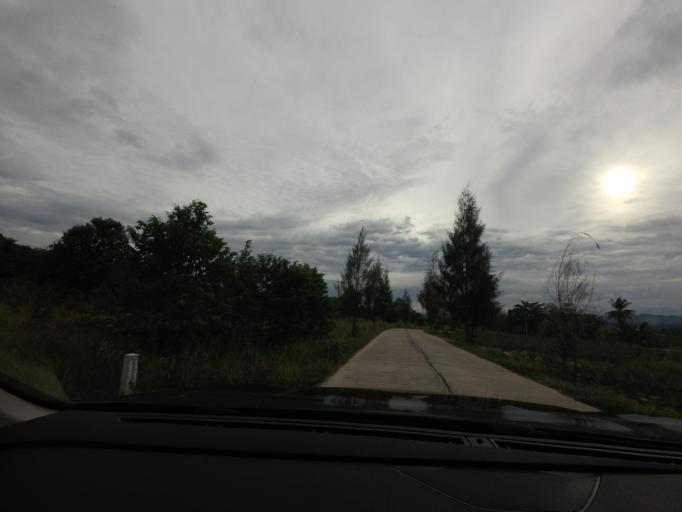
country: TH
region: Prachuap Khiri Khan
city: Hua Hin
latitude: 12.4819
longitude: 99.9403
